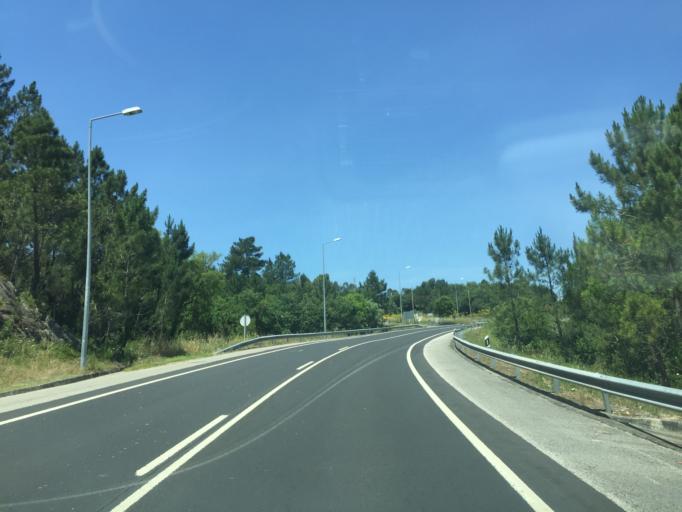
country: PT
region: Lisbon
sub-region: Mafra
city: Venda do Pinheiro
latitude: 38.8994
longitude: -9.2046
